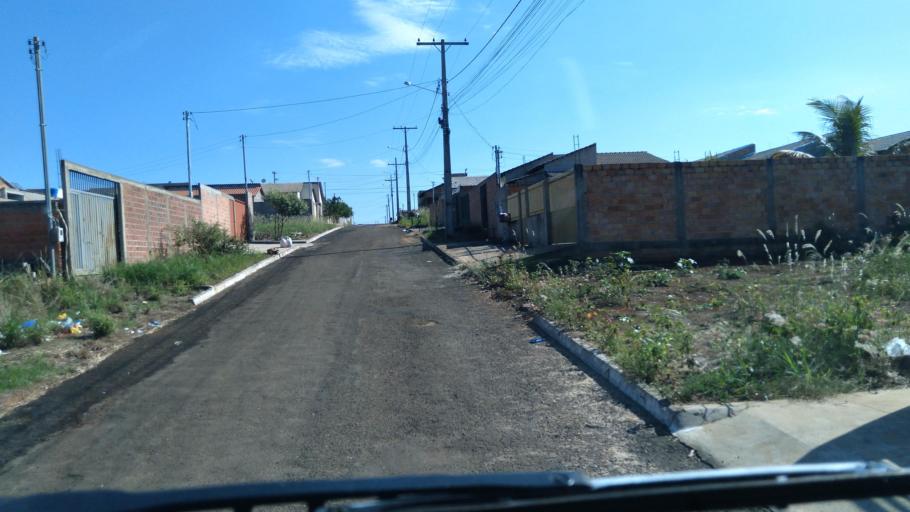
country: BR
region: Goias
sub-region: Mineiros
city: Mineiros
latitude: -17.5759
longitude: -52.5744
